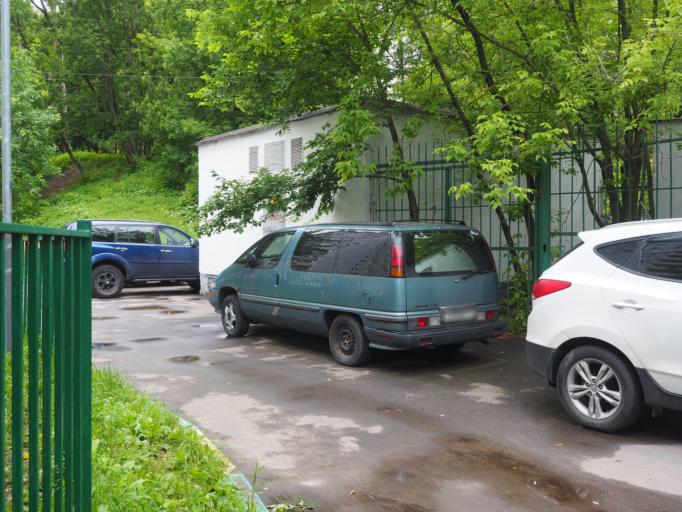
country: RU
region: Moscow
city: Vorob'yovo
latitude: 55.7287
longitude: 37.5271
